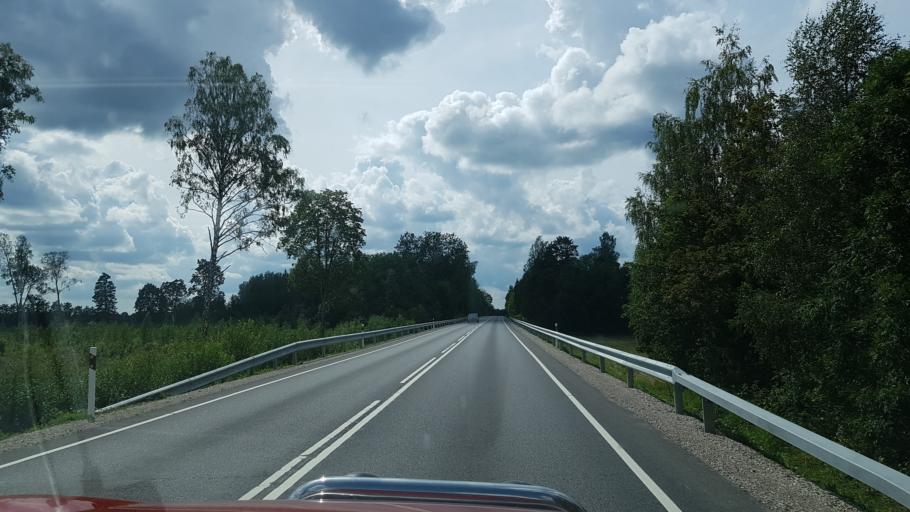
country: EE
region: Raplamaa
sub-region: Maerjamaa vald
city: Marjamaa
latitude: 58.9041
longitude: 24.2752
